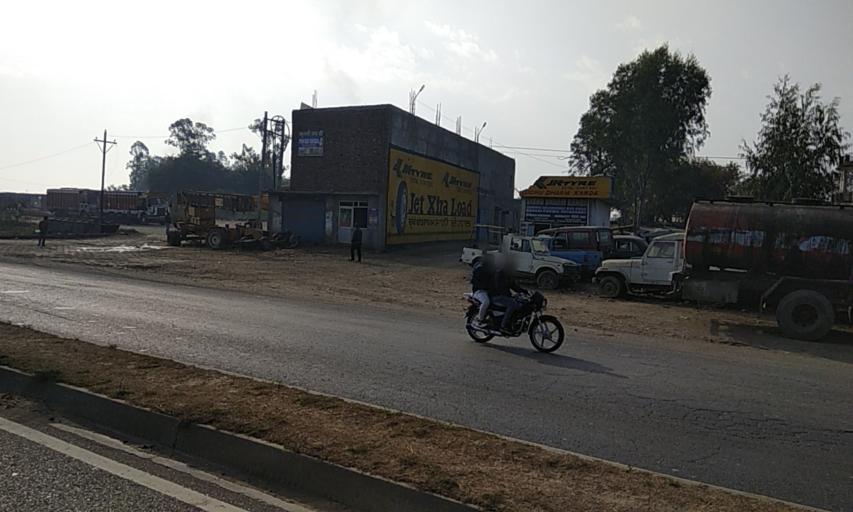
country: IN
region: Punjab
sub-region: Pathankot
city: Pathankot
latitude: 32.2581
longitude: 75.6347
